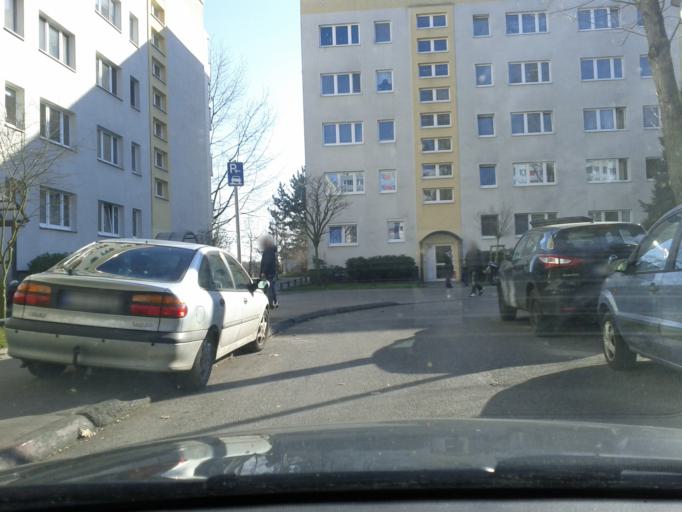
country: DE
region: Berlin
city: Friedrichsfelde
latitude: 52.5122
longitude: 13.5287
